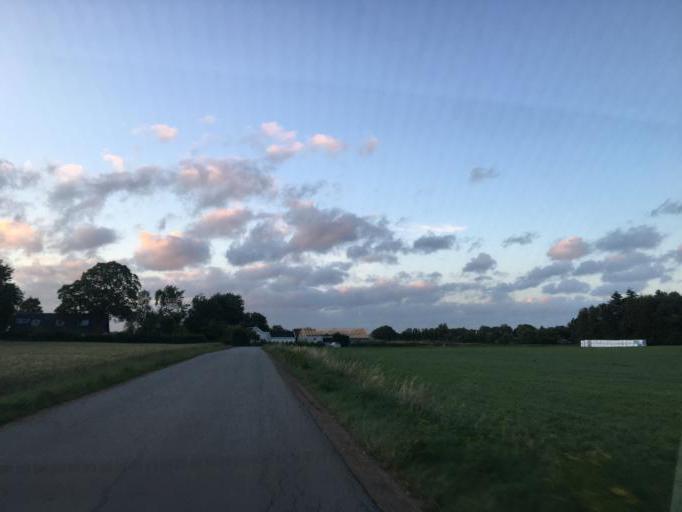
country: DK
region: Zealand
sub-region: Koge Kommune
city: Ejby
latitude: 55.5218
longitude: 12.0929
